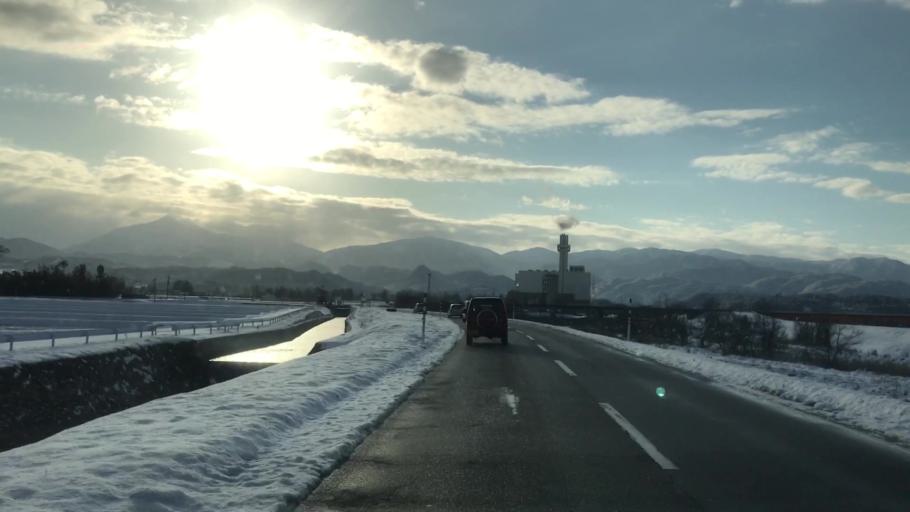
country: JP
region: Toyama
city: Kamiichi
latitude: 36.6302
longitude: 137.2977
